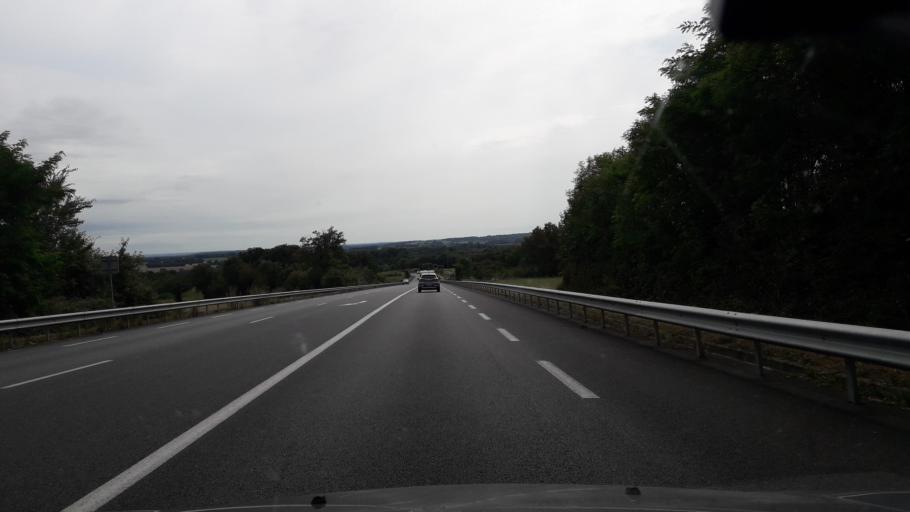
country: FR
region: Poitou-Charentes
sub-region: Departement de la Charente
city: Saint-Claud
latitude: 45.9044
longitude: 0.4842
